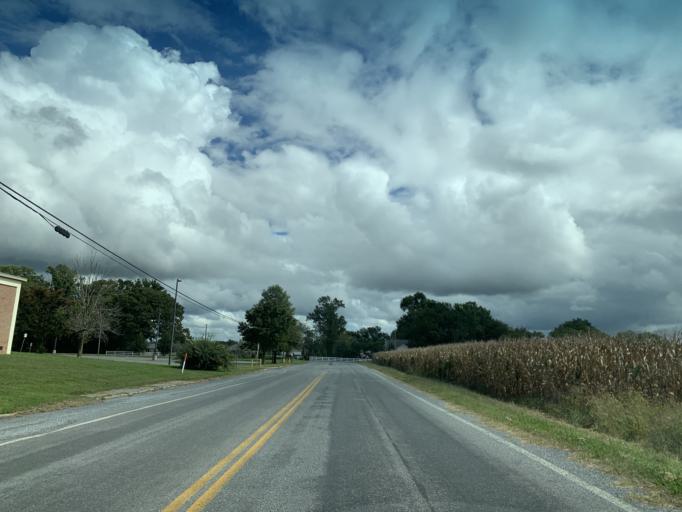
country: US
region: Maryland
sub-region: Caroline County
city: Denton
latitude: 38.9076
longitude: -75.8410
